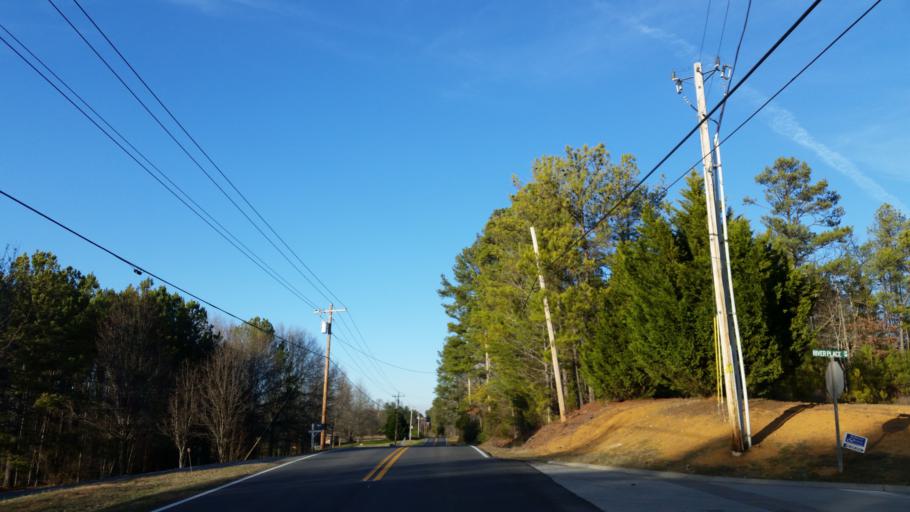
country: US
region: Georgia
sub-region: Gordon County
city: Calhoun
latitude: 34.5400
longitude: -84.9745
